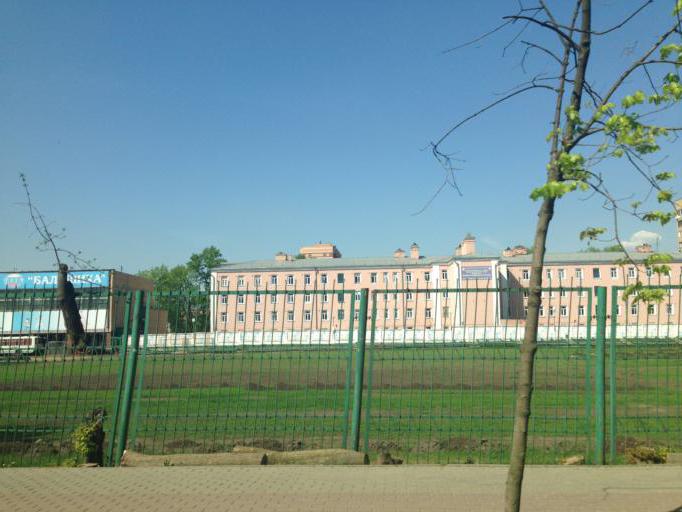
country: RU
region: Moskovskaya
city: Balashikha
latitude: 55.8152
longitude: 37.9668
